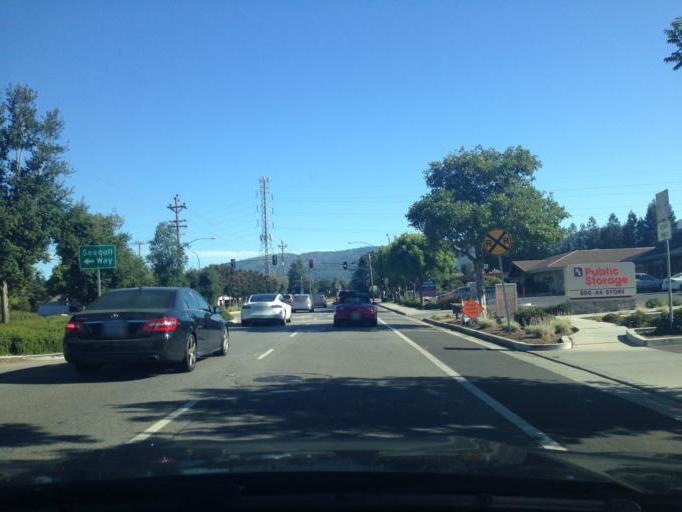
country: US
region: California
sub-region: Santa Clara County
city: Saratoga
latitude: 37.2900
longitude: -122.0325
